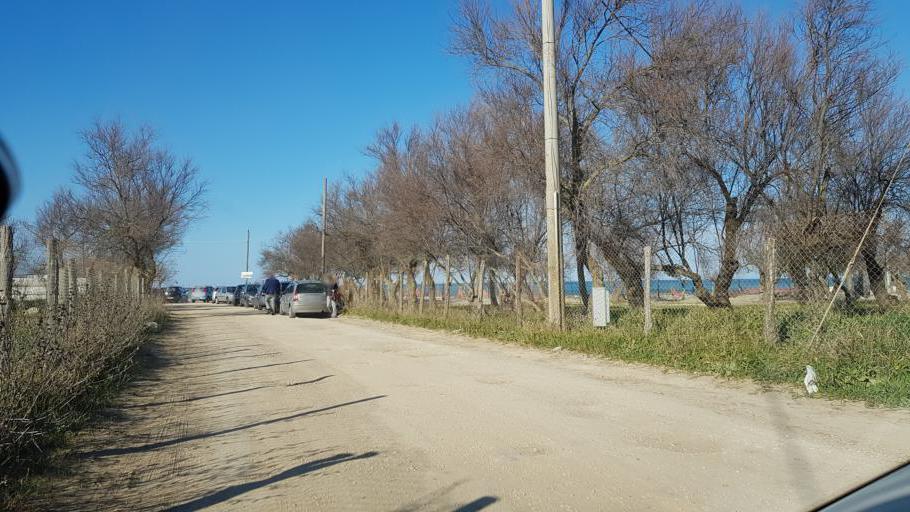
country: IT
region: Apulia
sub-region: Provincia di Brindisi
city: San Vito dei Normanni
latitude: 40.6940
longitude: 17.8272
